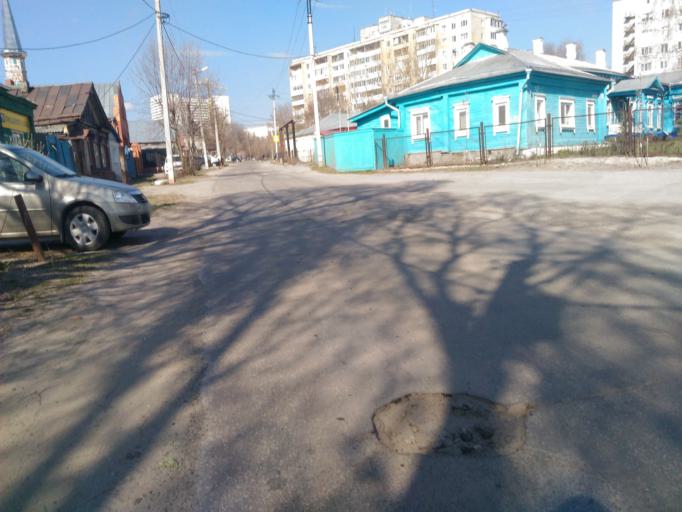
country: RU
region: Ulyanovsk
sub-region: Ulyanovskiy Rayon
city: Ulyanovsk
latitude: 54.3301
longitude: 48.3838
